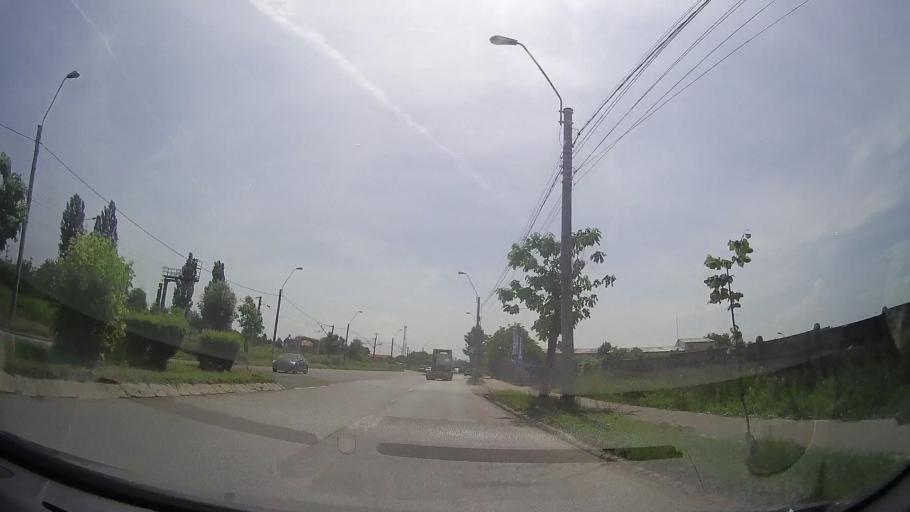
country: RO
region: Hunedoara
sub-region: Municipiul Deva
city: Deva
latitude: 45.8929
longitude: 22.9031
